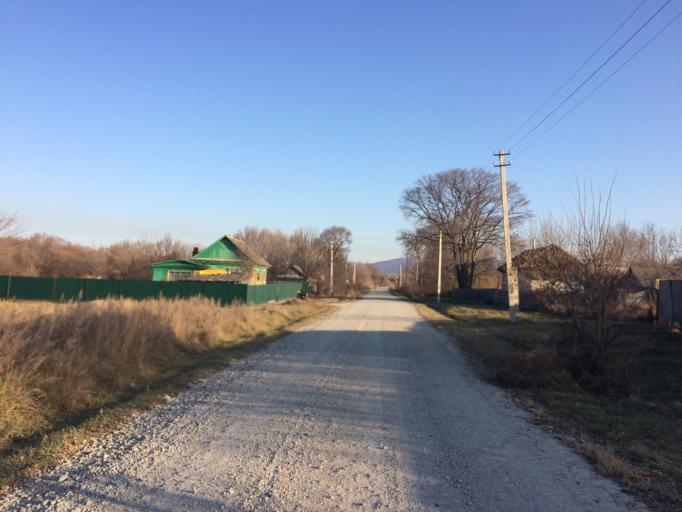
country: RU
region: Primorskiy
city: Ivanovka
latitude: 43.9566
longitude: 132.4801
